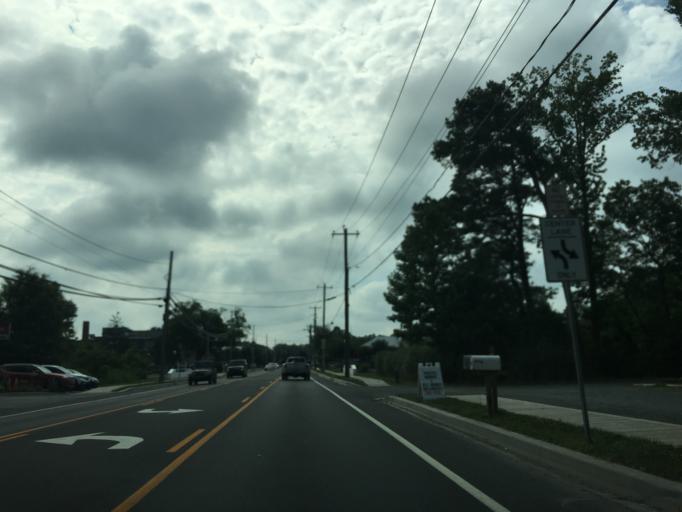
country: US
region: Delaware
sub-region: Sussex County
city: Ocean View
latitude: 38.5453
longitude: -75.0973
